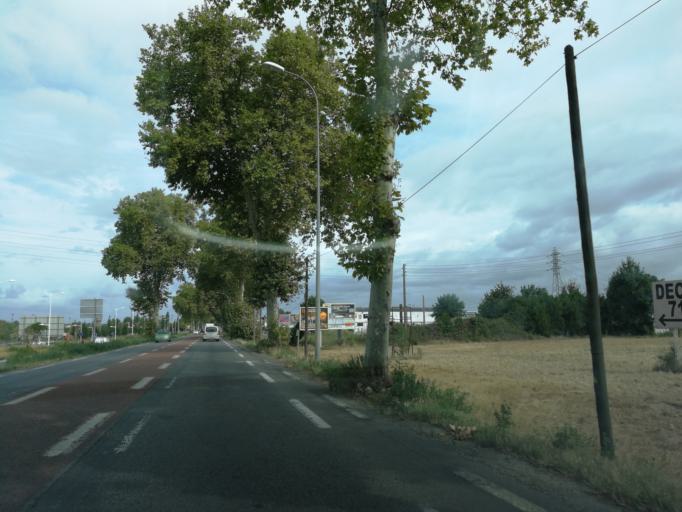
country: FR
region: Midi-Pyrenees
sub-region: Departement de la Haute-Garonne
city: Saint-Alban
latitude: 43.6914
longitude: 1.4032
